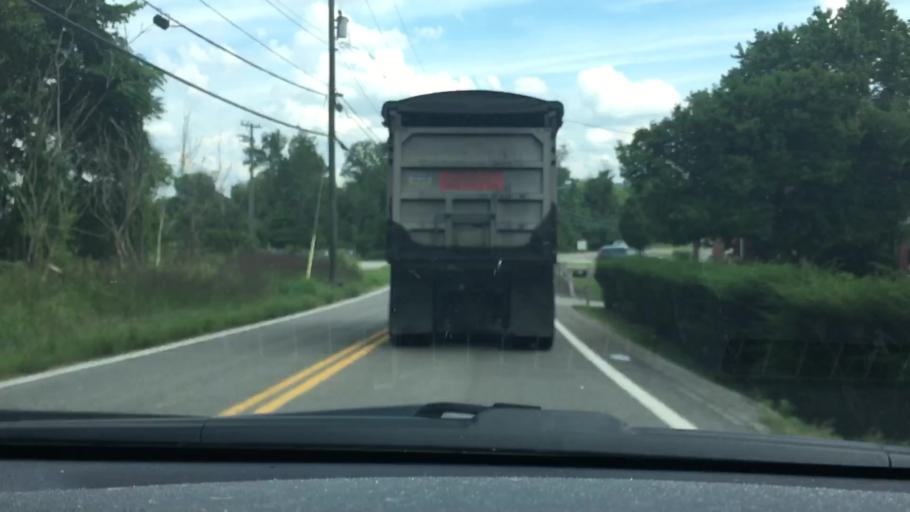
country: US
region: Pennsylvania
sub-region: Allegheny County
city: Jefferson Hills
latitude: 40.2566
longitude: -79.9328
